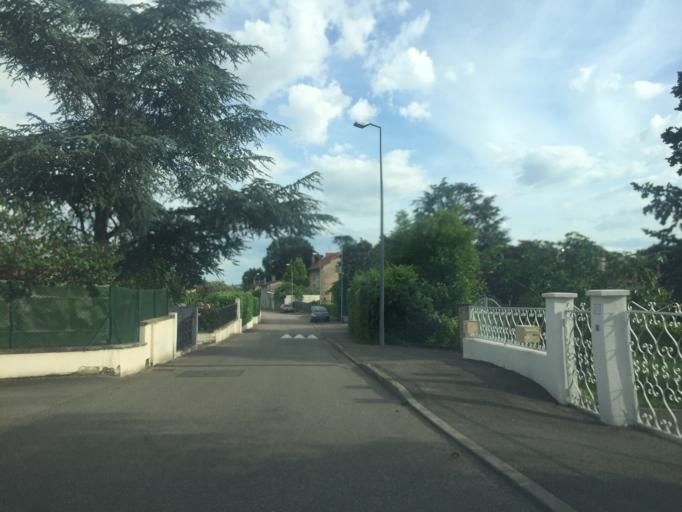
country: FR
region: Rhone-Alpes
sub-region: Departement de l'Ain
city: Saint-Maurice-de-Beynost
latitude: 45.8370
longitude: 4.9912
